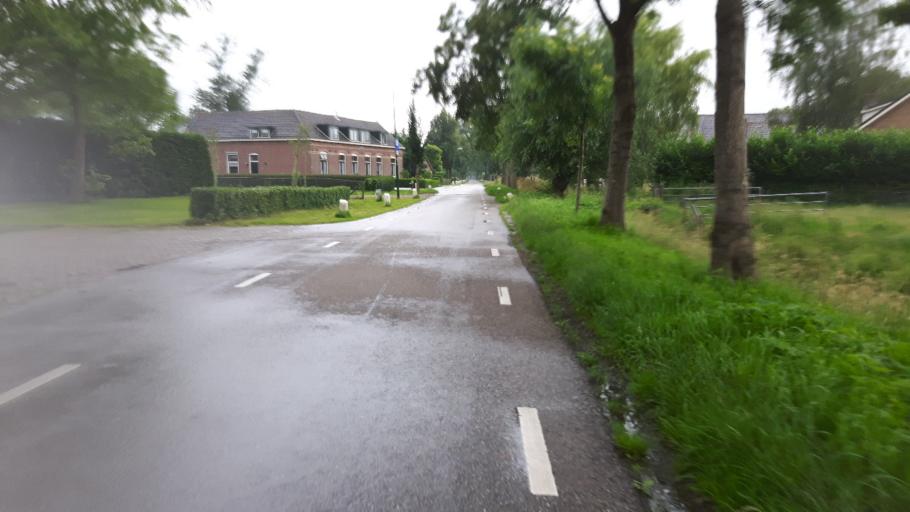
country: NL
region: Utrecht
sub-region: Gemeente Montfoort
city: Montfoort
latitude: 52.0372
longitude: 4.9635
